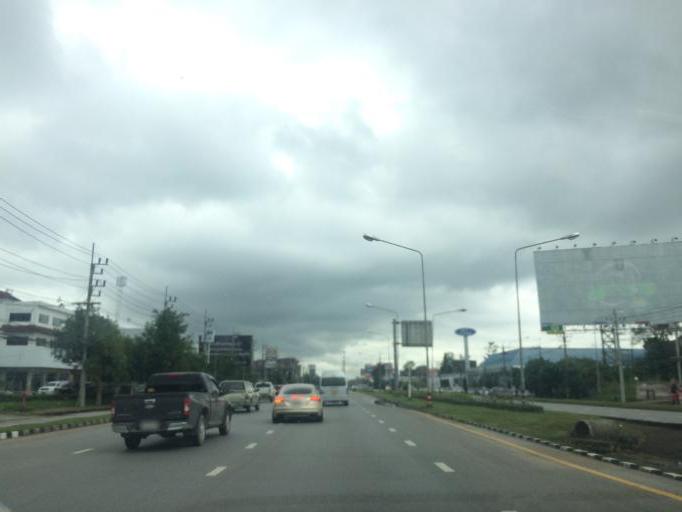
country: TH
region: Chiang Rai
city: Chiang Rai
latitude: 19.8806
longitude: 99.8335
